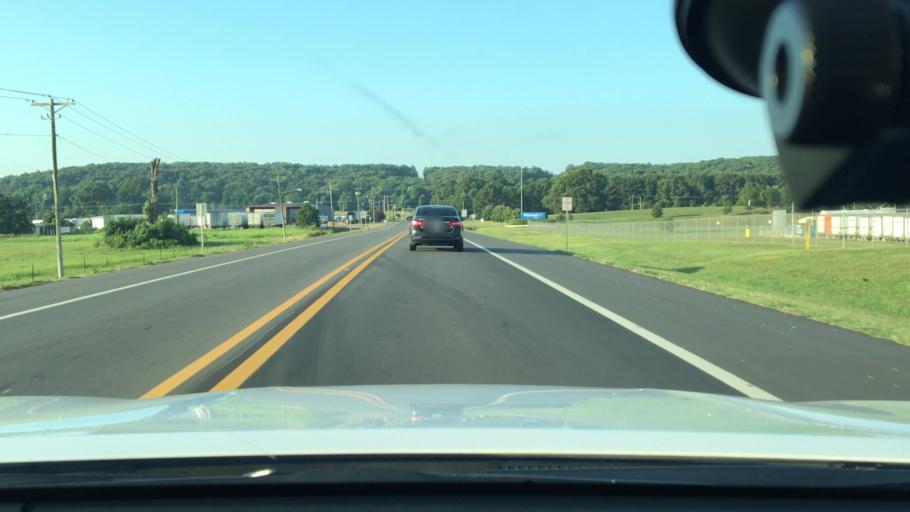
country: US
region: Arkansas
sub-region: Johnson County
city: Clarksville
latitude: 35.4301
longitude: -93.5295
